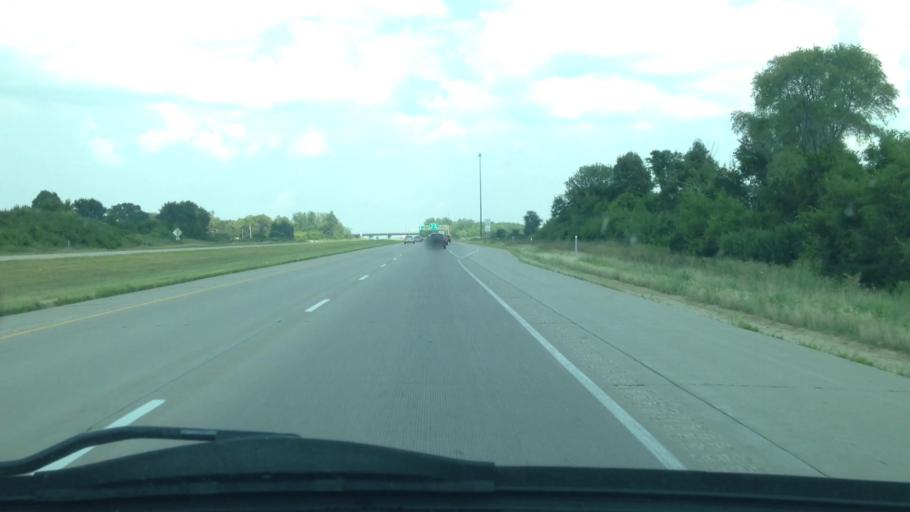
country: US
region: Iowa
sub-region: Black Hawk County
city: Elk Run Heights
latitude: 42.4492
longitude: -92.2072
